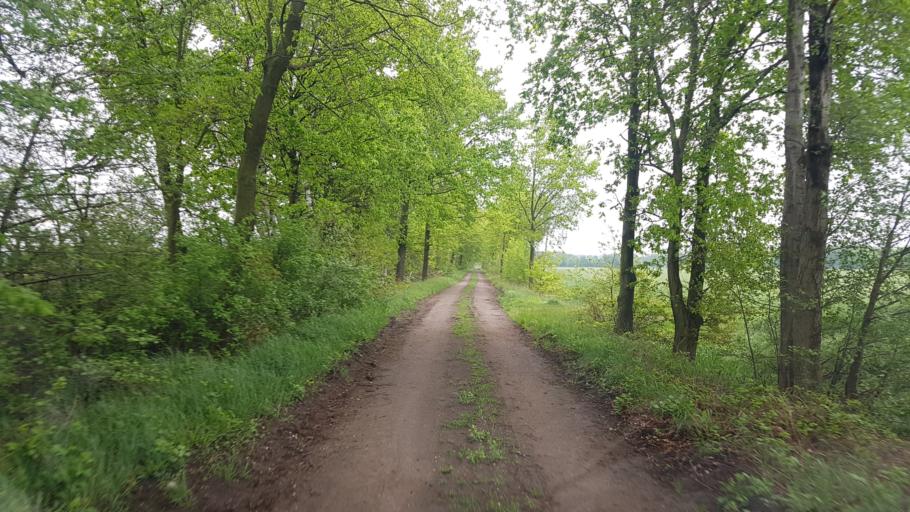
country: DE
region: Brandenburg
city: Elsterwerda
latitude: 51.4387
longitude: 13.5436
